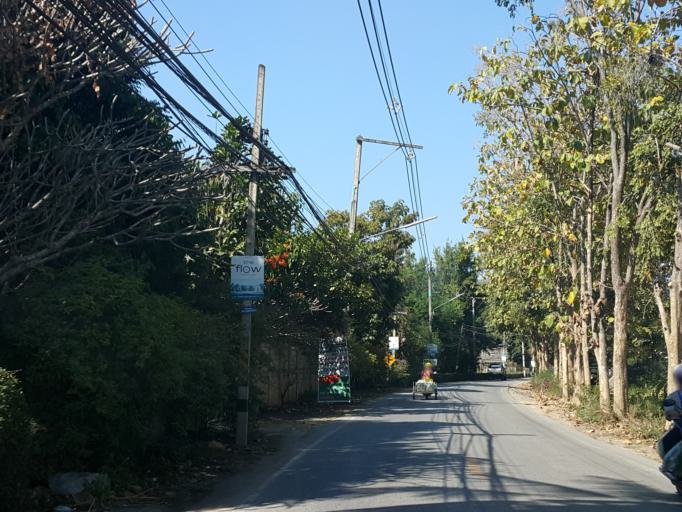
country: TH
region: Chiang Mai
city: San Sai
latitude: 18.8500
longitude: 98.9874
